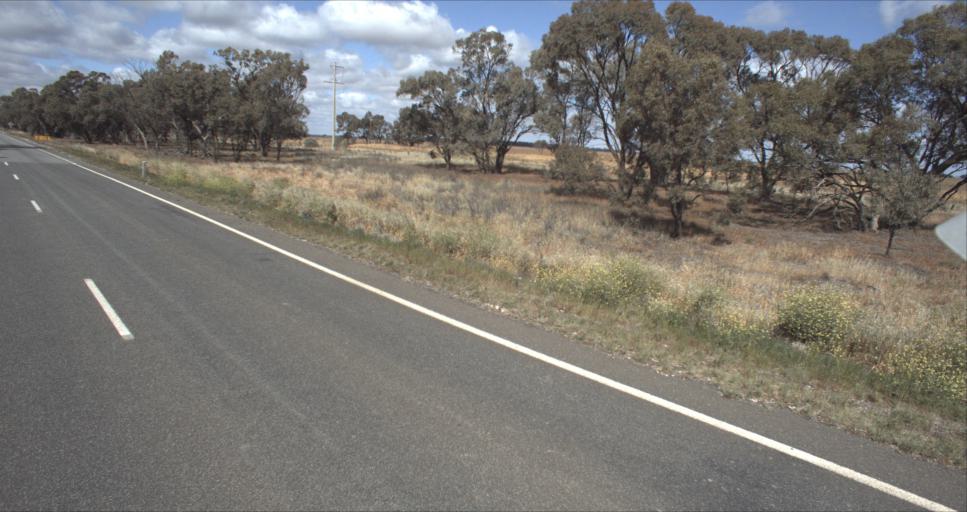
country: AU
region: New South Wales
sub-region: Murrumbidgee Shire
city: Darlington Point
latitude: -34.5615
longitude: 146.1689
